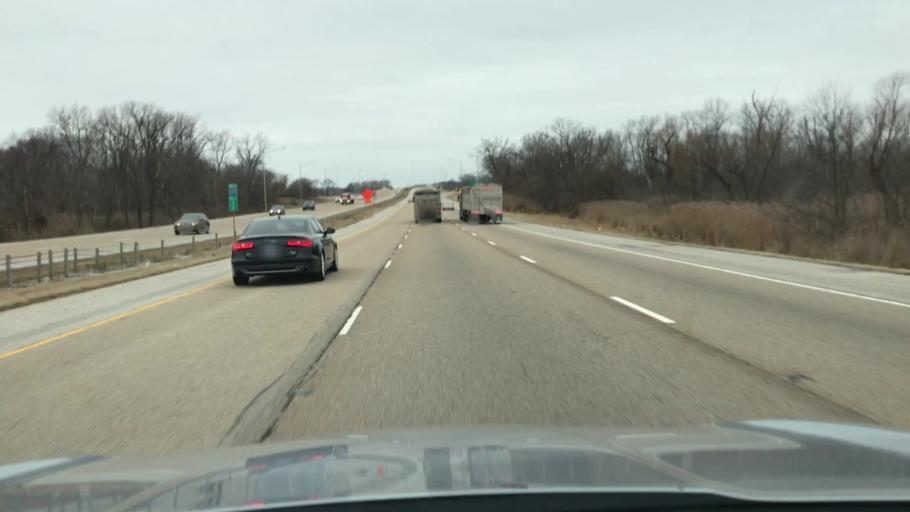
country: US
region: Illinois
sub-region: Saint Clair County
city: Fairmont City
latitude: 38.6640
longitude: -90.0844
